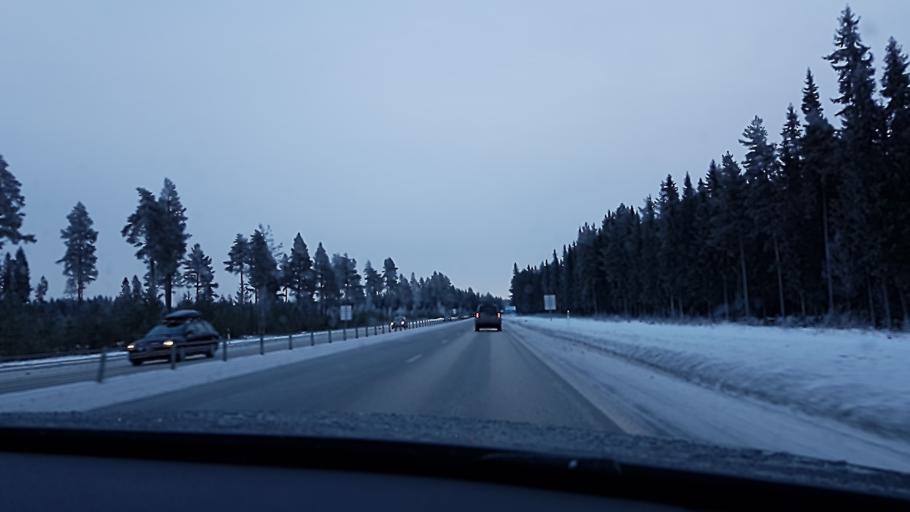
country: SE
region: Jaemtland
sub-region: OEstersunds Kommun
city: Brunflo
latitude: 63.1339
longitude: 14.7891
